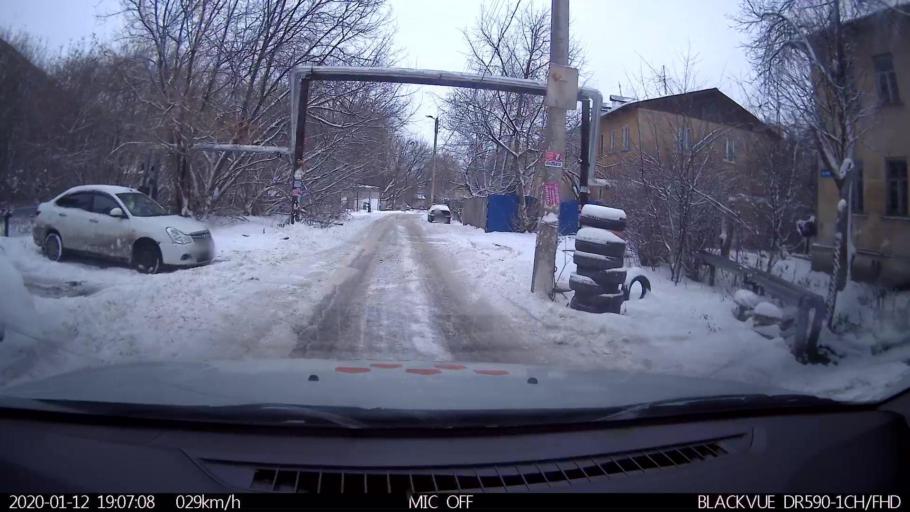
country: RU
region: Nizjnij Novgorod
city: Nizhniy Novgorod
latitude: 56.3316
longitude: 43.9130
